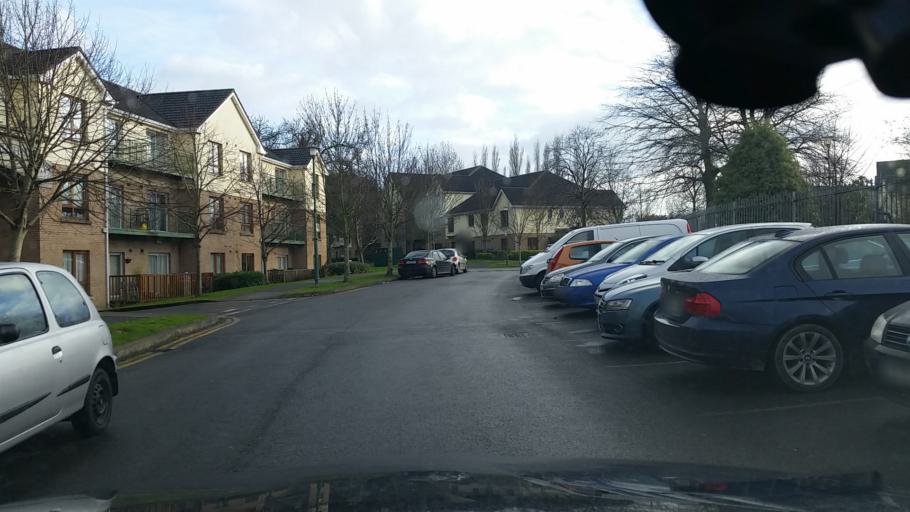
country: IE
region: Leinster
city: Beaumont
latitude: 53.3992
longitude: -6.2283
